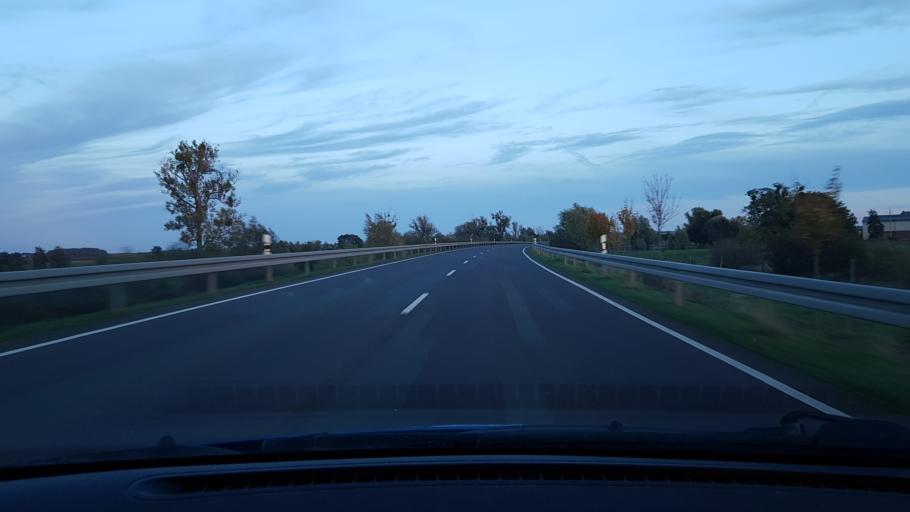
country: DE
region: Saxony-Anhalt
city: Gommern
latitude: 52.0760
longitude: 11.8702
